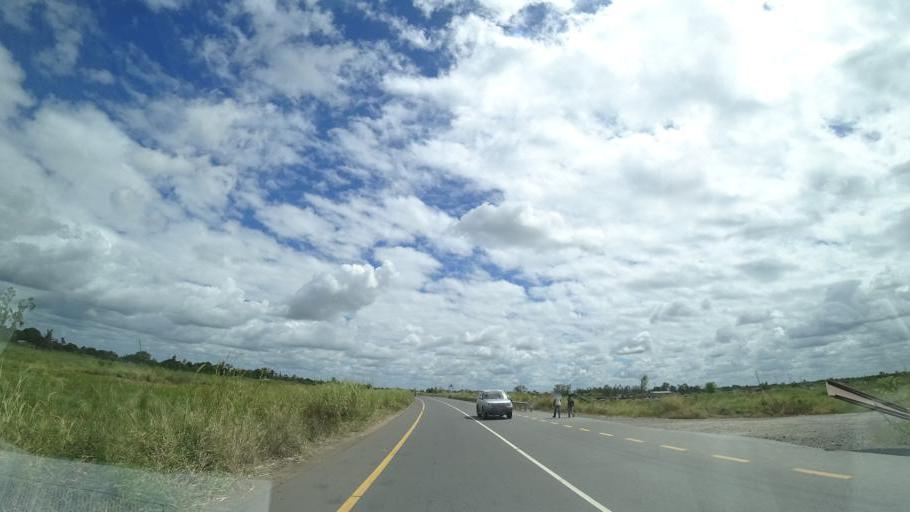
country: MZ
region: Sofala
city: Dondo
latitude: -19.3977
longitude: 34.4270
